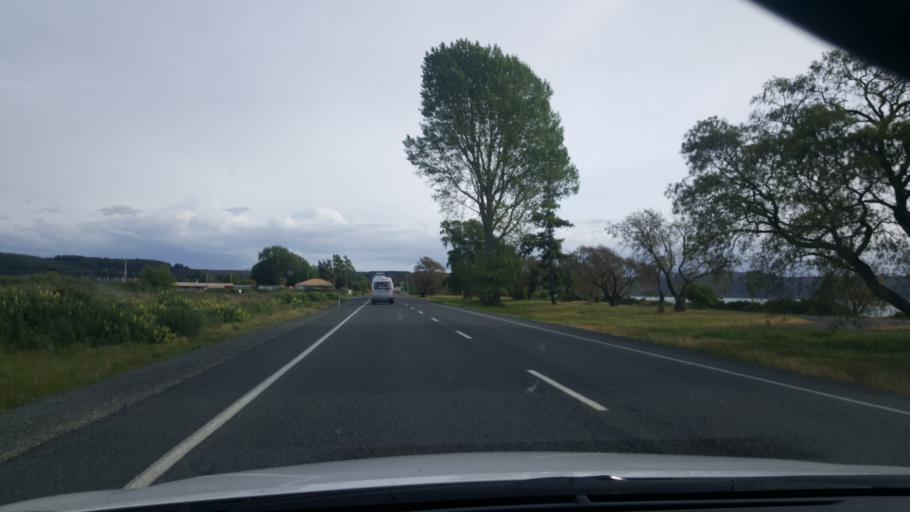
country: NZ
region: Waikato
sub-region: Taupo District
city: Taupo
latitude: -38.7752
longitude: 176.0765
